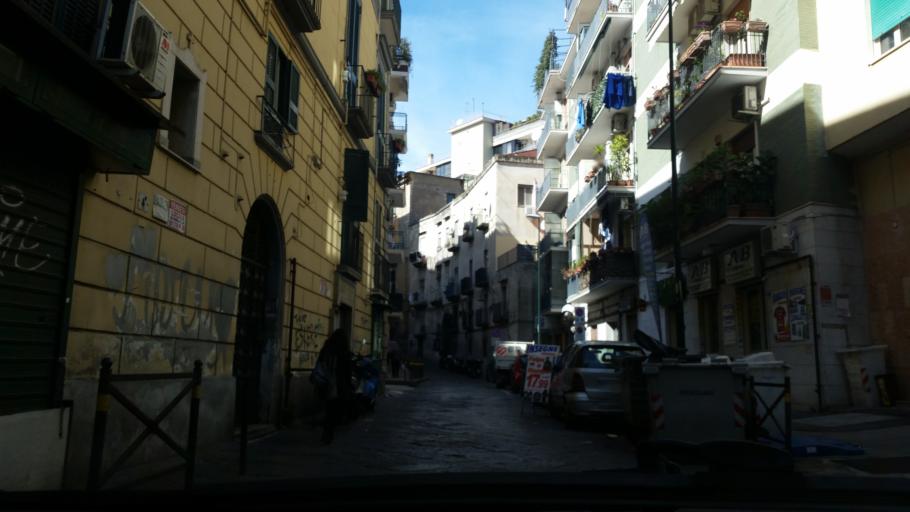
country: IT
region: Campania
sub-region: Provincia di Napoli
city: Napoli
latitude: 40.8516
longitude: 14.2348
